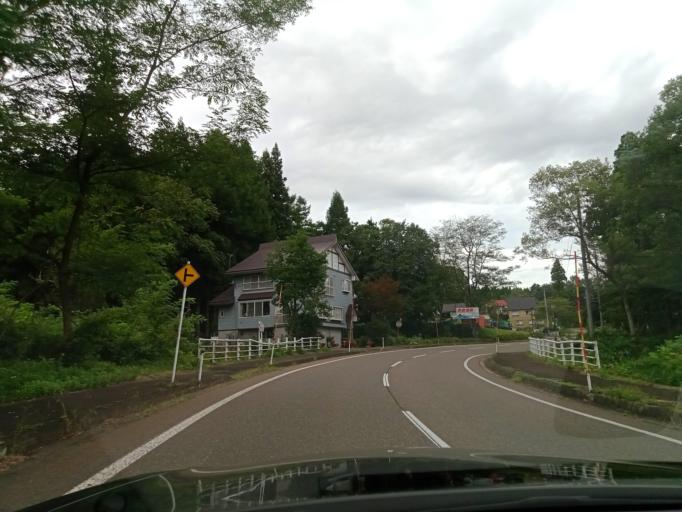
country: JP
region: Niigata
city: Arai
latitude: 36.8776
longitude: 138.2000
